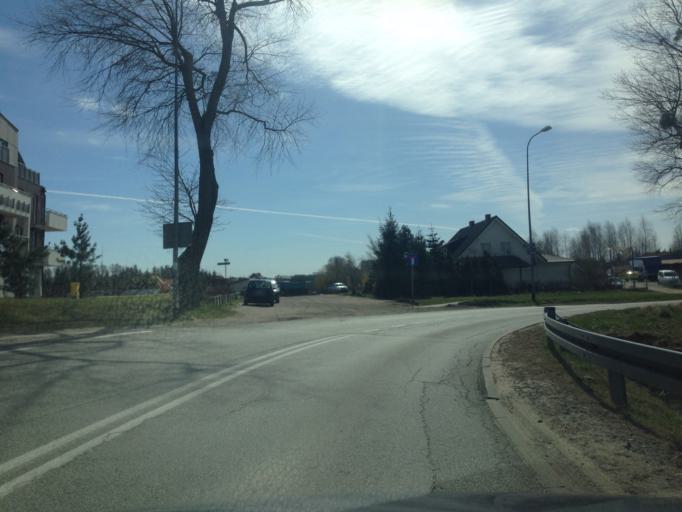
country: PL
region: Pomeranian Voivodeship
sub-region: Powiat wejherowski
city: Bojano
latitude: 54.4938
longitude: 18.4299
